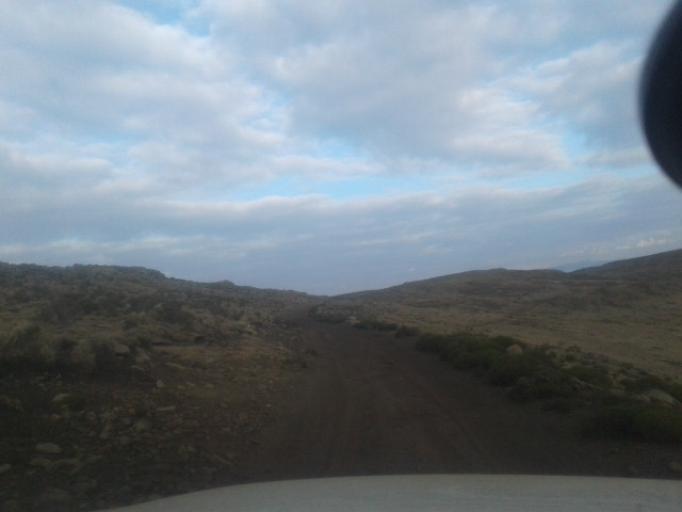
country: LS
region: Thaba-Tseka
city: Thaba-Tseka
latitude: -29.4154
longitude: 28.2718
